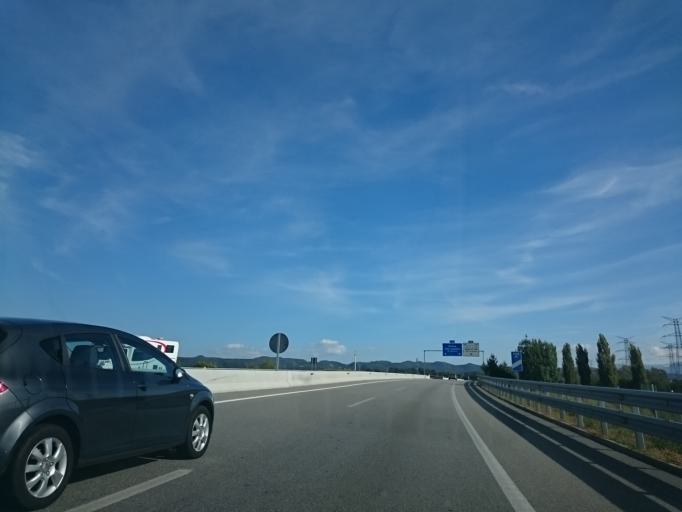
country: ES
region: Catalonia
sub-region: Provincia de Barcelona
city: Vic
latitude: 41.9585
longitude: 2.2834
